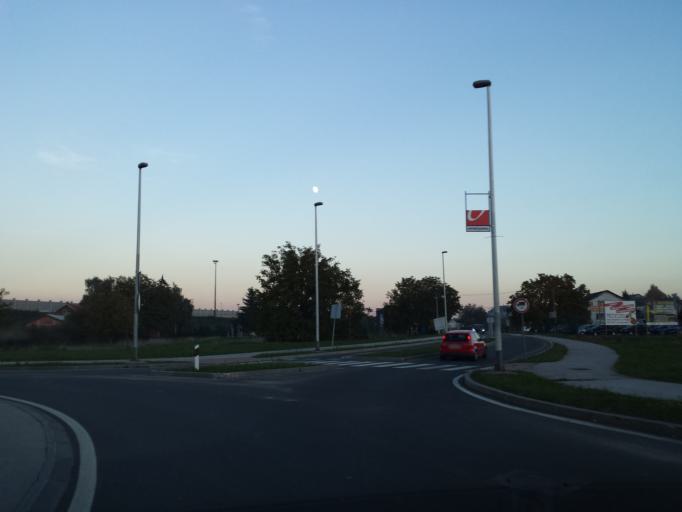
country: HR
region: Zagrebacka
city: Bestovje
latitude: 45.7999
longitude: 15.7792
